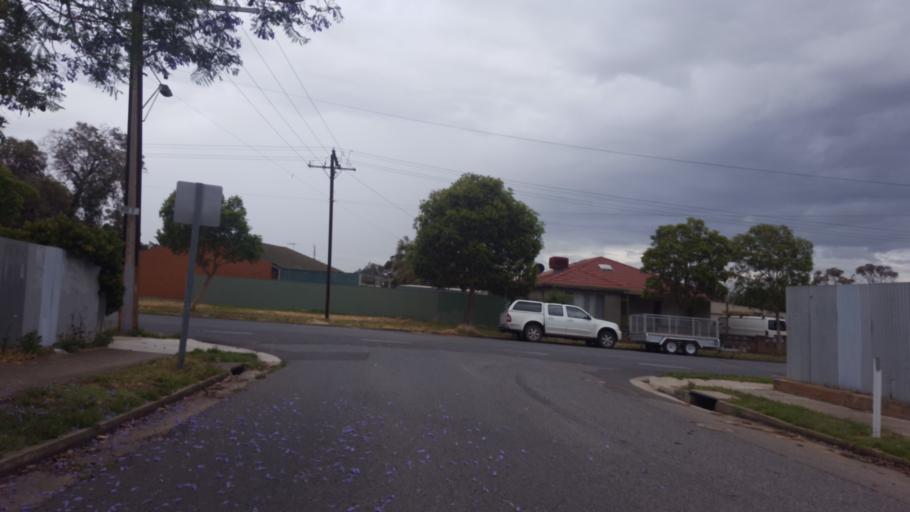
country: AU
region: South Australia
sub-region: Port Adelaide Enfield
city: Alberton
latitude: -34.8488
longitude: 138.5324
